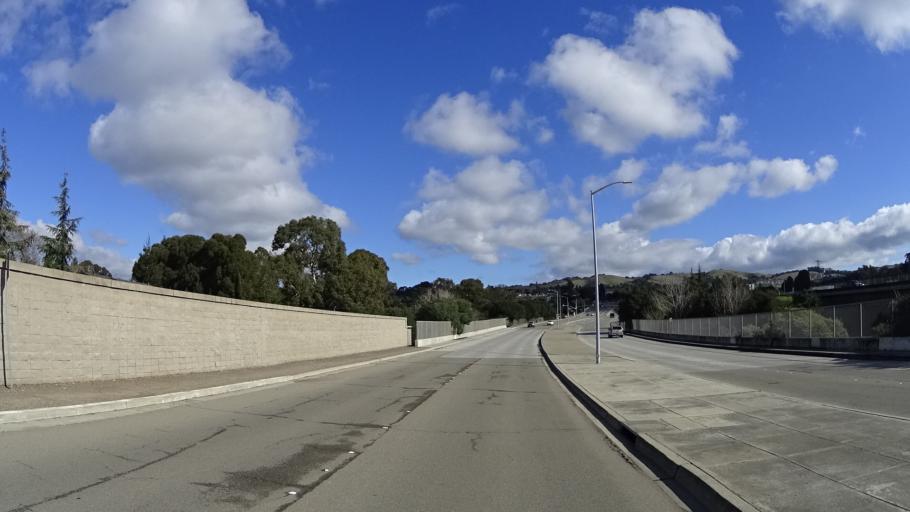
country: US
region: California
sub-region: Alameda County
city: Fairview
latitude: 37.6941
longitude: -122.0602
